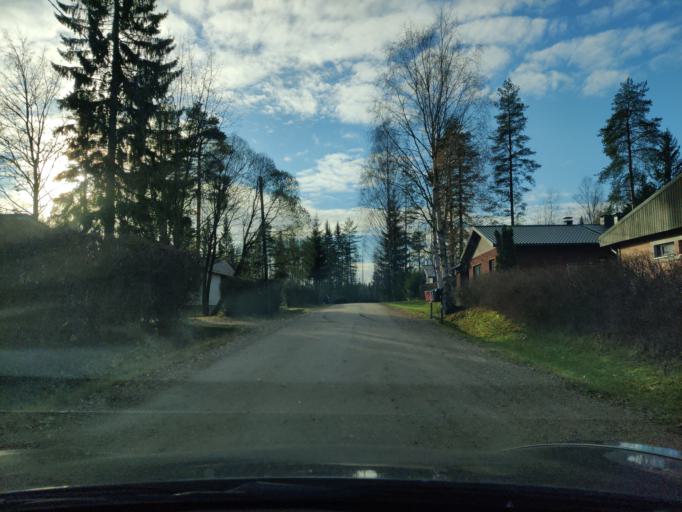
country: FI
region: Northern Savo
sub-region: Ylae-Savo
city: Kiuruvesi
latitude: 63.6447
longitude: 26.6373
